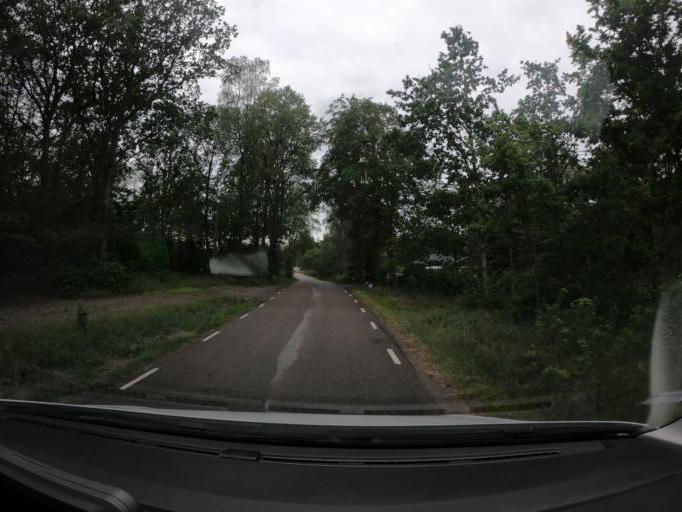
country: SE
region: Skane
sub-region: Klippans Kommun
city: Klippan
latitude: 56.2671
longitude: 13.1438
